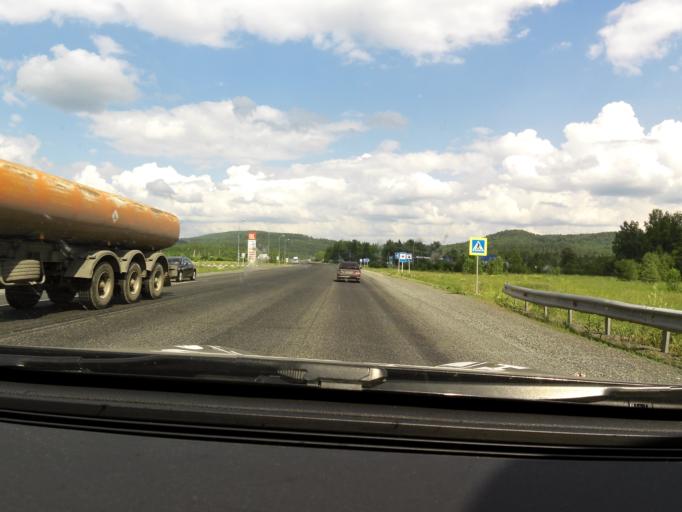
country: RU
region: Sverdlovsk
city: Arti
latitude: 56.7914
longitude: 58.6044
